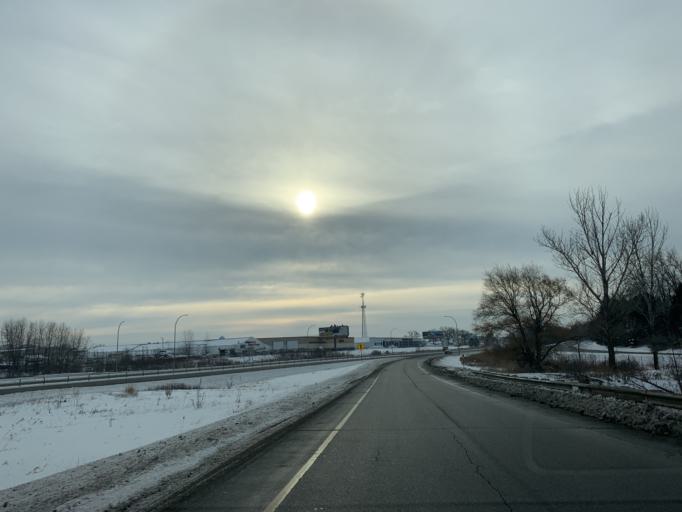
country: US
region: Minnesota
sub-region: Chisago County
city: Wyoming
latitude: 45.3355
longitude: -93.0056
